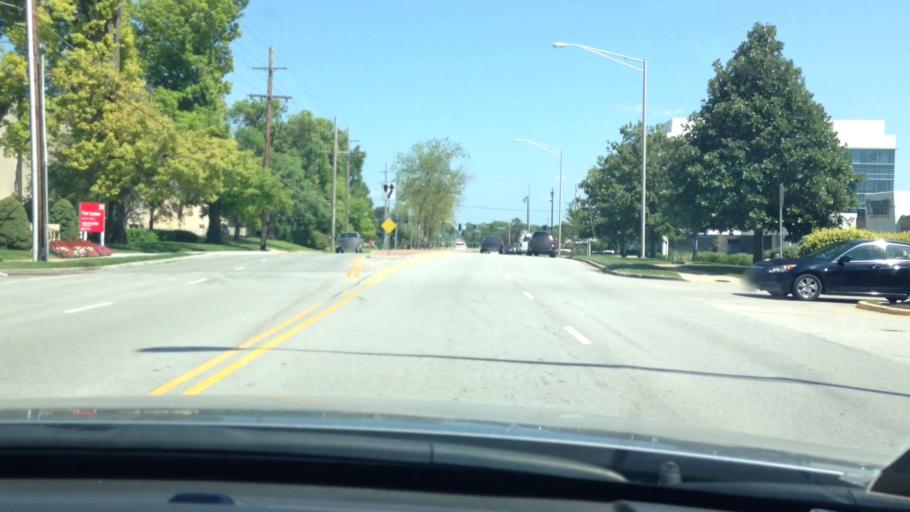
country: US
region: Kansas
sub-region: Johnson County
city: Overland Park
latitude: 38.9568
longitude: -94.6512
